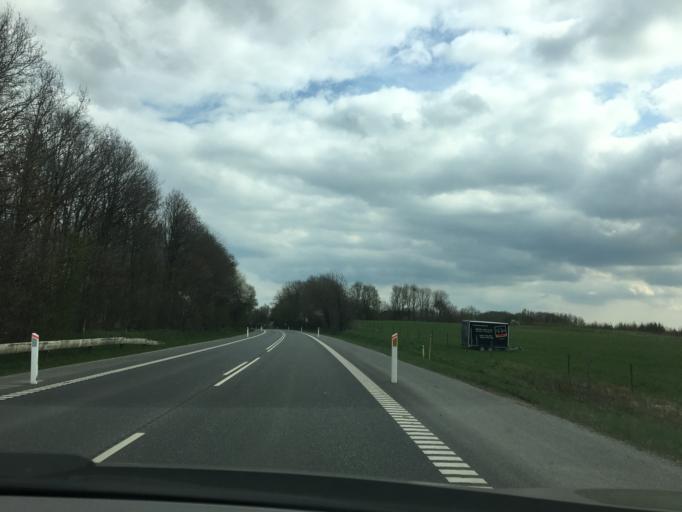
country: DK
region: Central Jutland
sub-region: Horsens Kommune
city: Braedstrup
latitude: 55.9542
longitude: 9.6256
